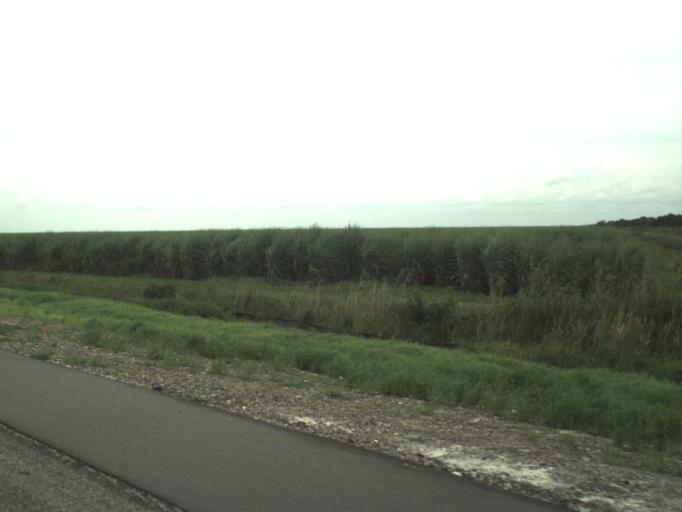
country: US
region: Florida
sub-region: Palm Beach County
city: Loxahatchee Groves
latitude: 26.7151
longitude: -80.4256
